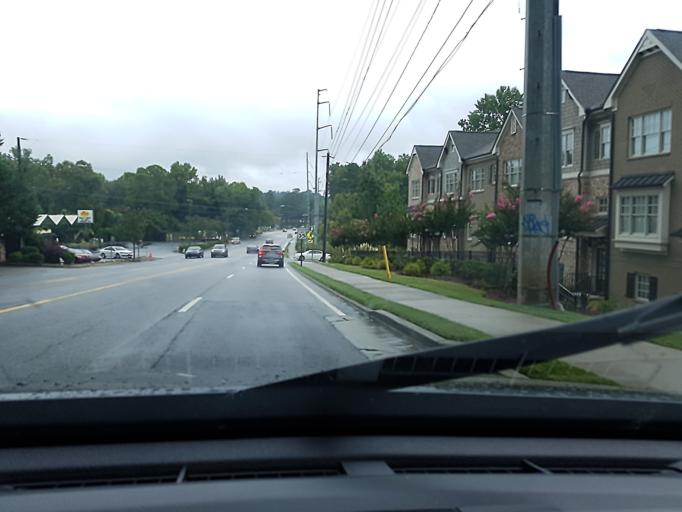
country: US
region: Georgia
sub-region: DeKalb County
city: North Atlanta
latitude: 33.8642
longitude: -84.3805
